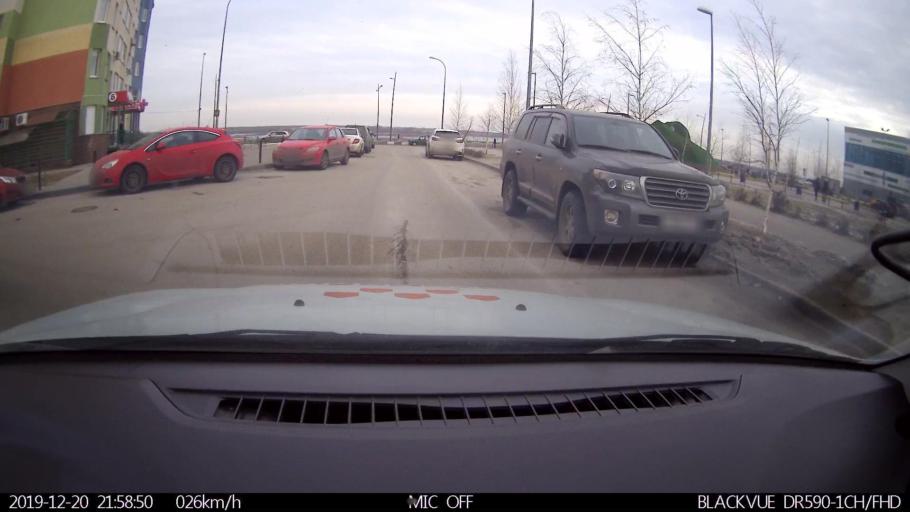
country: RU
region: Nizjnij Novgorod
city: Nizhniy Novgorod
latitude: 56.3413
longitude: 43.9550
